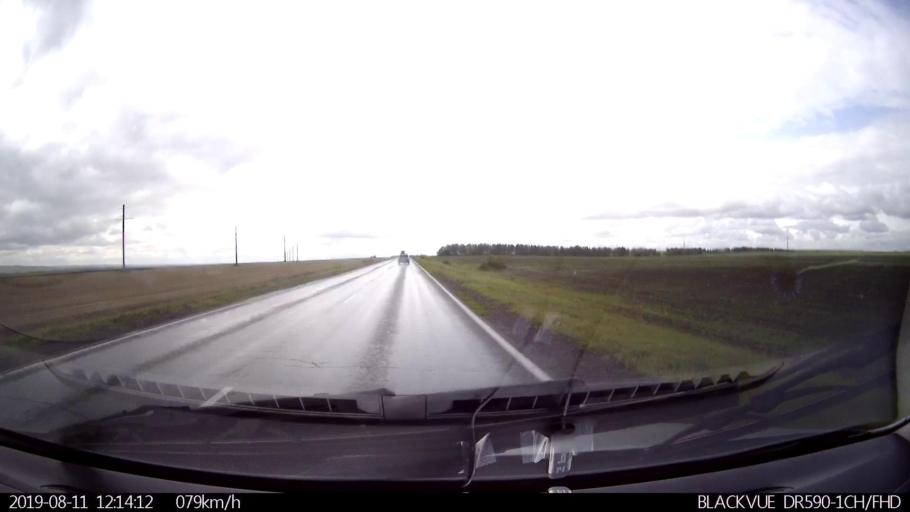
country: RU
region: Ulyanovsk
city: Ignatovka
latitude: 53.9543
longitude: 47.9830
